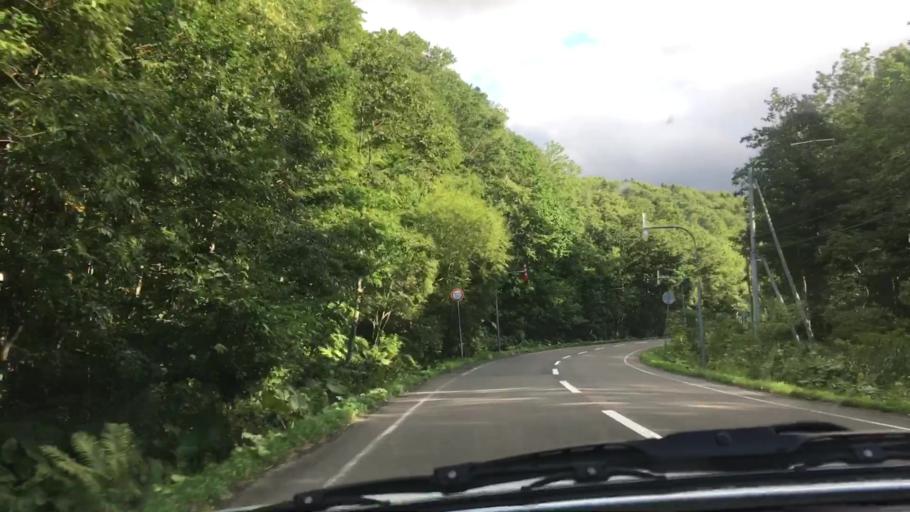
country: JP
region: Hokkaido
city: Shimo-furano
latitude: 43.0974
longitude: 142.6858
